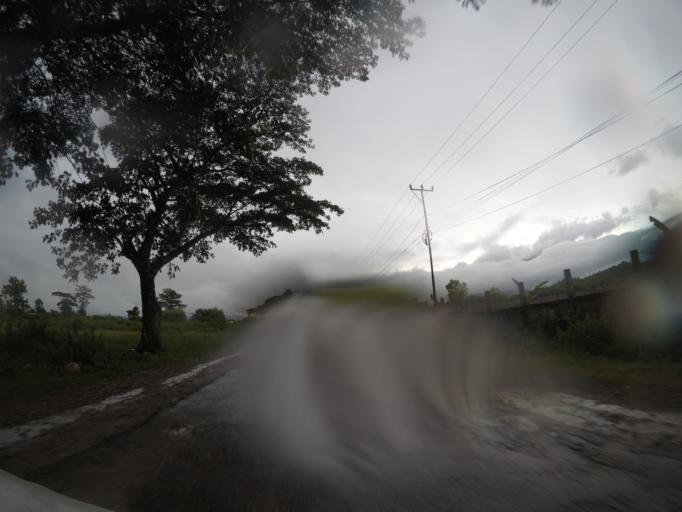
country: TL
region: Bobonaro
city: Maliana
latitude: -8.9912
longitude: 125.1842
